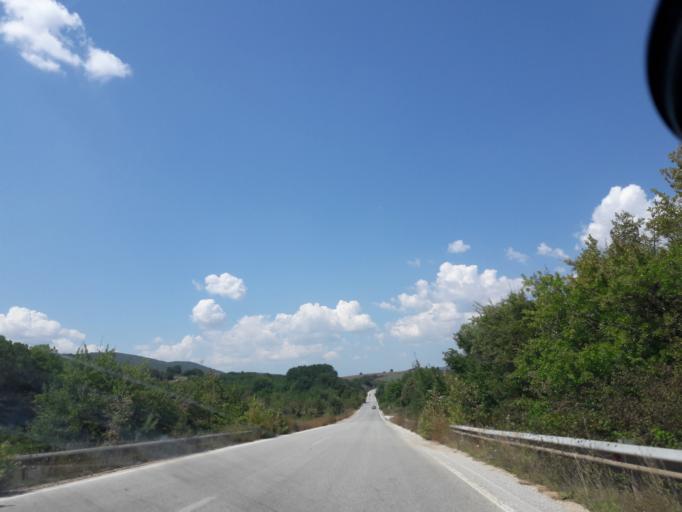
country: GR
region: Central Macedonia
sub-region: Nomos Chalkidikis
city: Polygyros
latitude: 40.4610
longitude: 23.3894
